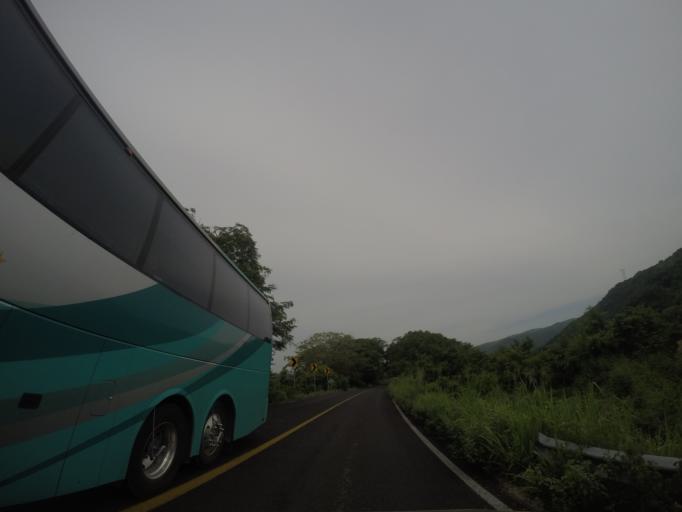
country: MX
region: Oaxaca
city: San Pedro Mixtepec
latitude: 15.9568
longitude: -97.2426
